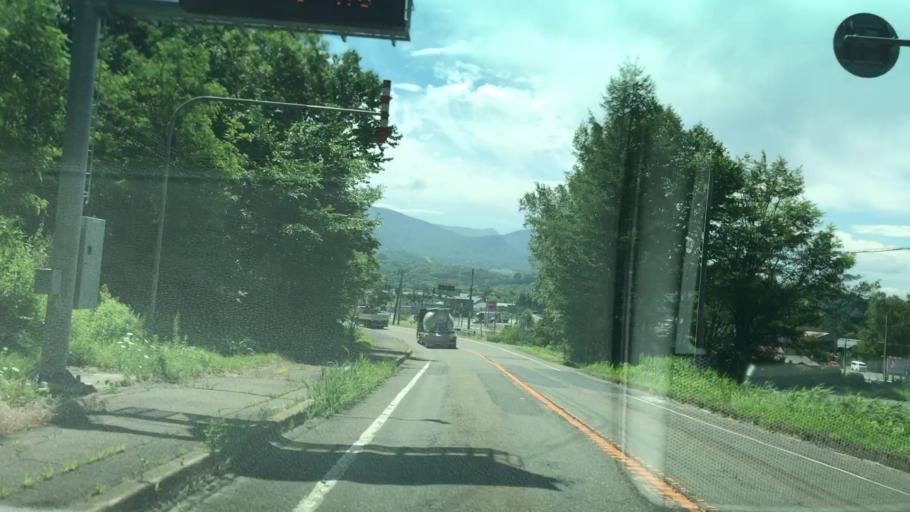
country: JP
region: Hokkaido
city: Shimo-furano
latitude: 42.8841
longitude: 142.4341
